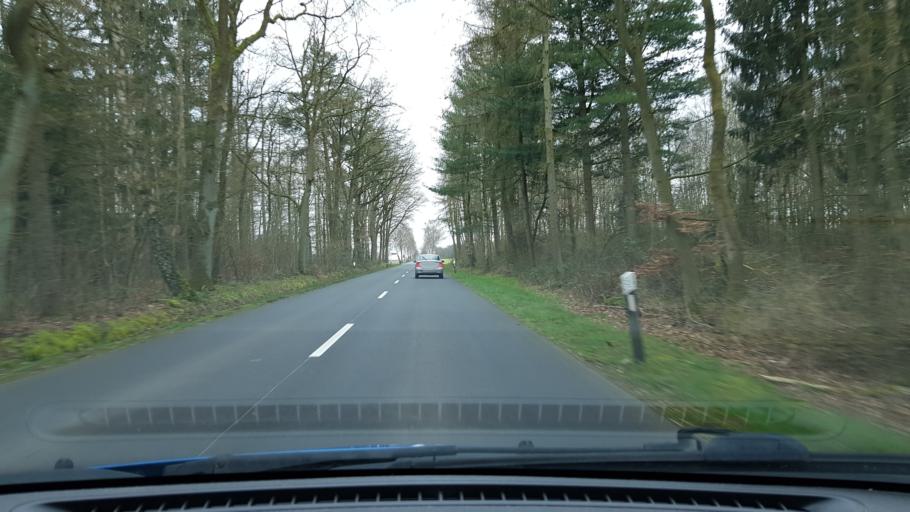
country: DE
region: Lower Saxony
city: Emmendorf
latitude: 53.0234
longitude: 10.6030
